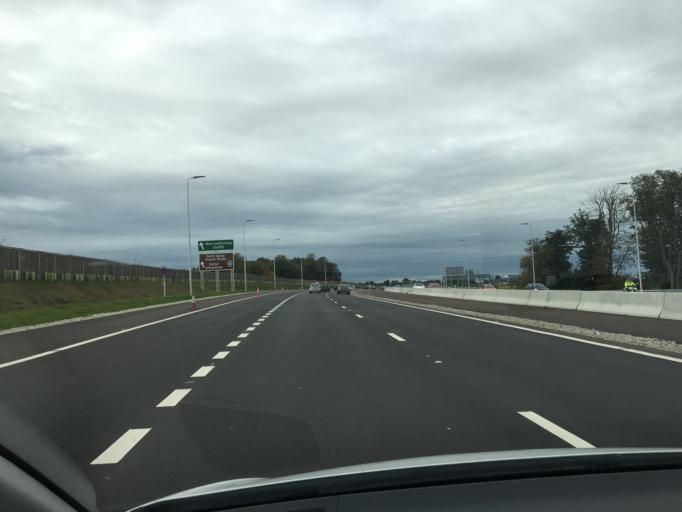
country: GB
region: Scotland
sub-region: Edinburgh
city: Queensferry
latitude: 55.9807
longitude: -3.4098
